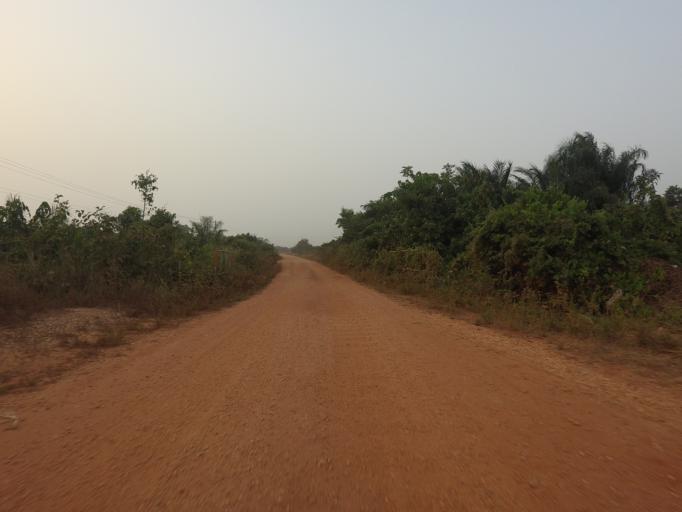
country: GH
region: Volta
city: Anloga
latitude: 5.9792
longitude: 0.6053
